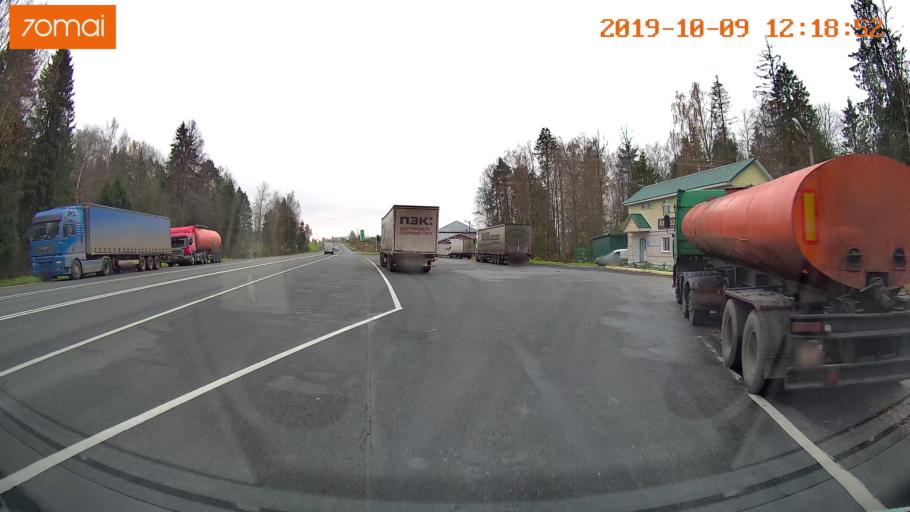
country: RU
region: Jaroslavl
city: Prechistoye
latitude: 58.4368
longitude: 40.3214
